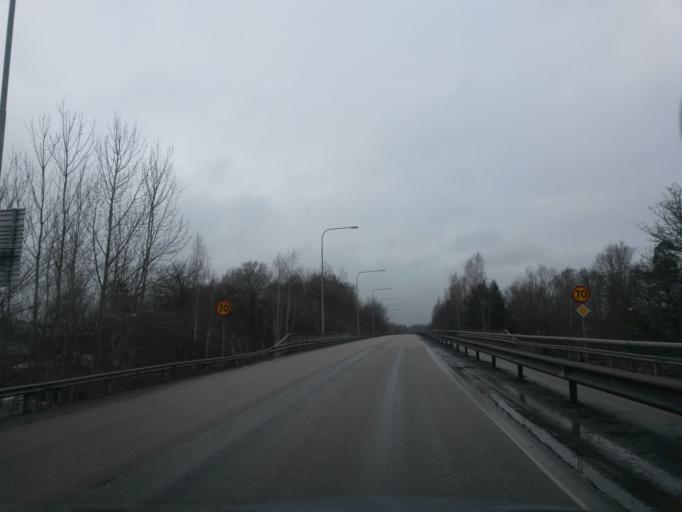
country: SE
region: Vaestra Goetaland
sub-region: Vanersborgs Kommun
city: Vargon
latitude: 58.3580
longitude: 12.3854
